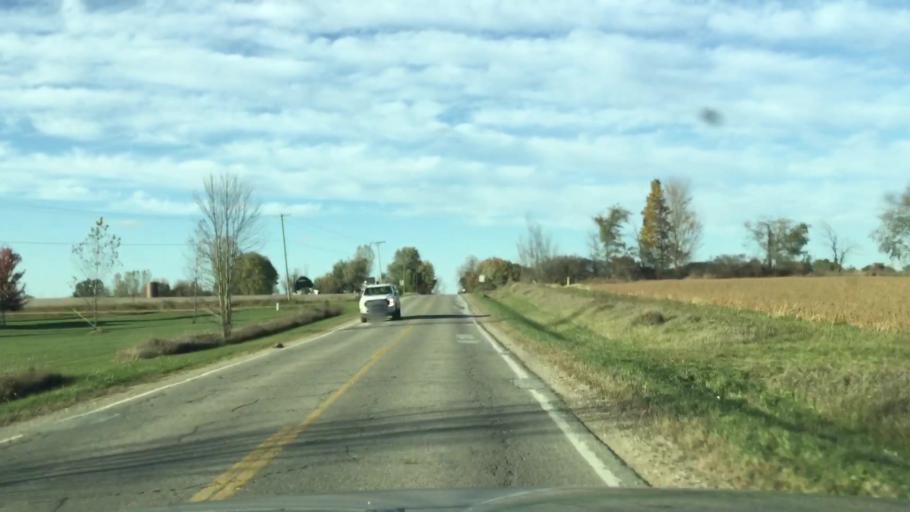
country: US
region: Michigan
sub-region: Lapeer County
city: North Branch
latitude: 43.2446
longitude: -83.1975
